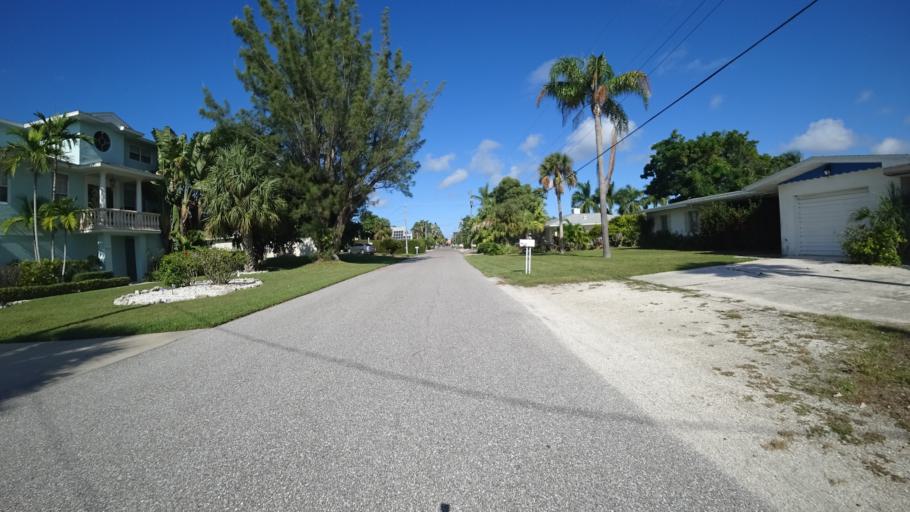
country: US
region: Florida
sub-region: Manatee County
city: Anna Maria
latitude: 27.5204
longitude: -82.7240
